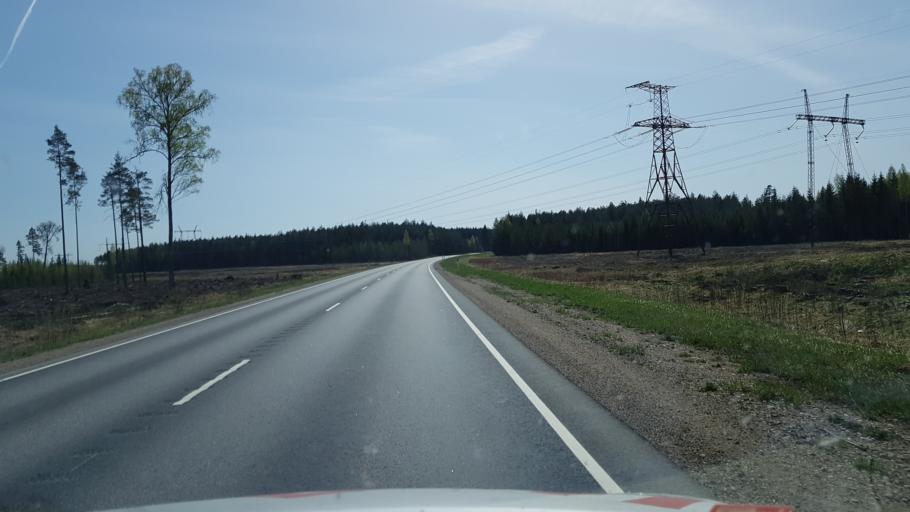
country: EE
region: Valgamaa
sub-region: Valga linn
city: Valga
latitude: 57.8808
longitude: 26.1625
